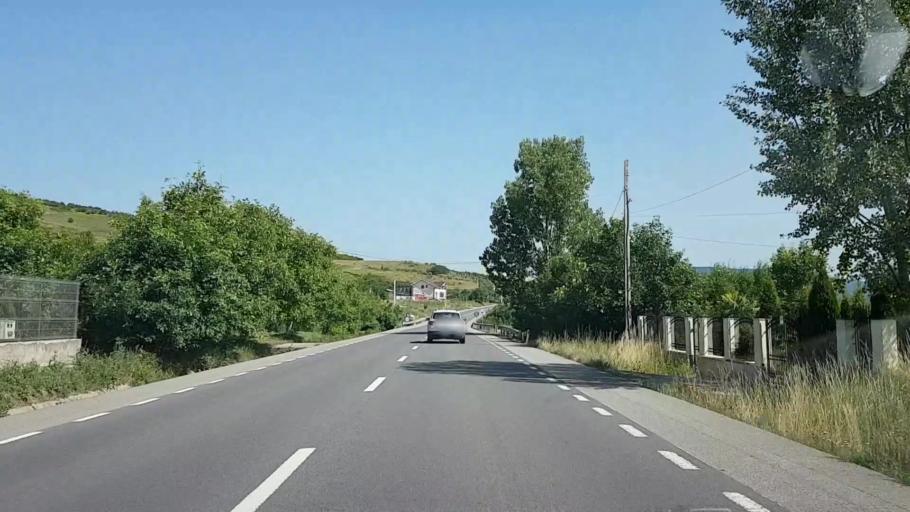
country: RO
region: Bistrita-Nasaud
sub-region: Comuna Sieu-Magherus
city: Sieu-Magherus
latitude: 47.0790
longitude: 24.3947
